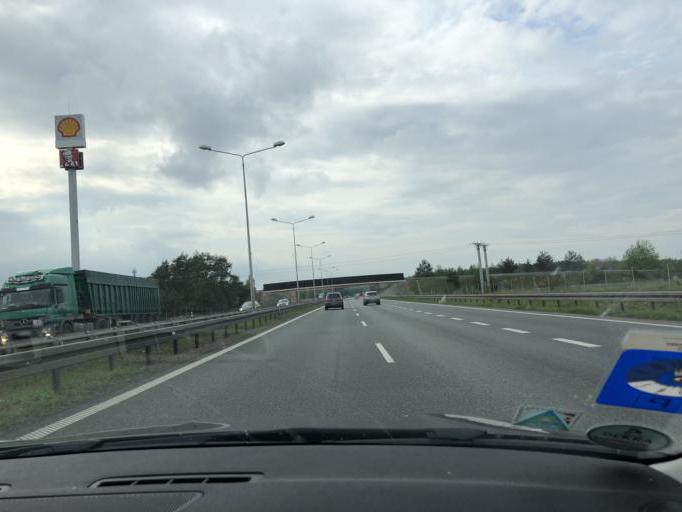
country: PL
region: Opole Voivodeship
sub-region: Powiat opolski
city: Niemodlin
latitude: 50.6781
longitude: 17.6517
